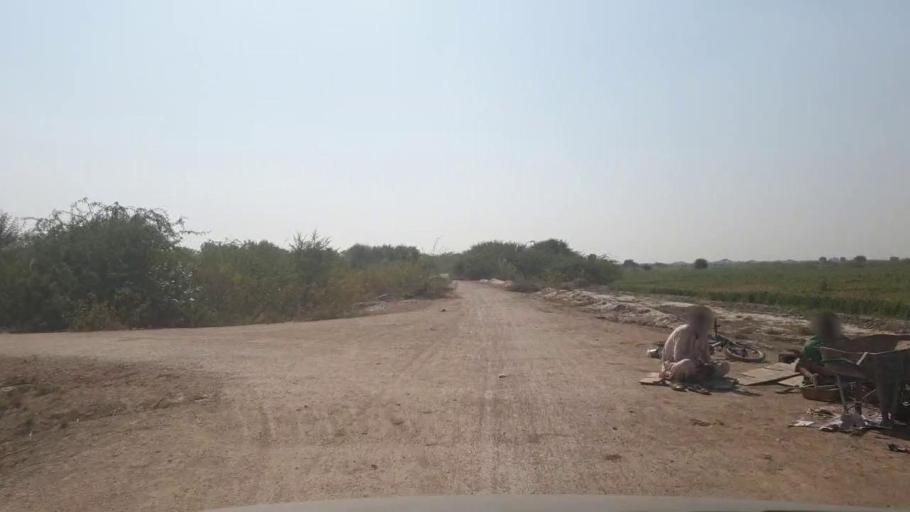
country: PK
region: Sindh
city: Chambar
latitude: 25.2268
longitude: 68.8207
